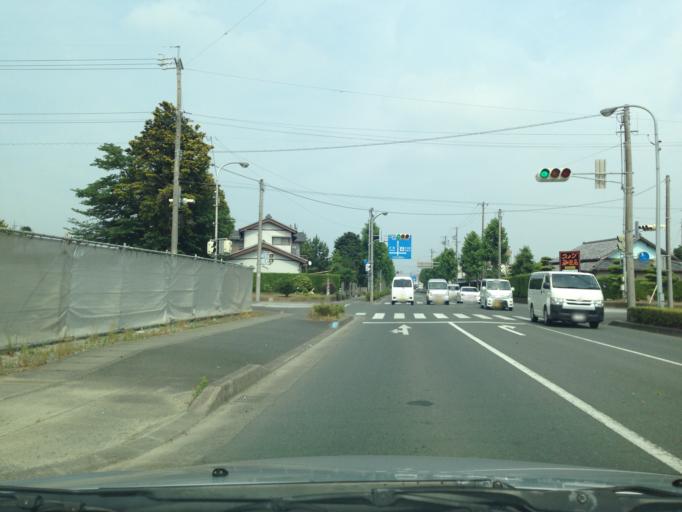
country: JP
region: Shizuoka
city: Hamakita
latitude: 34.8100
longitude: 137.7905
